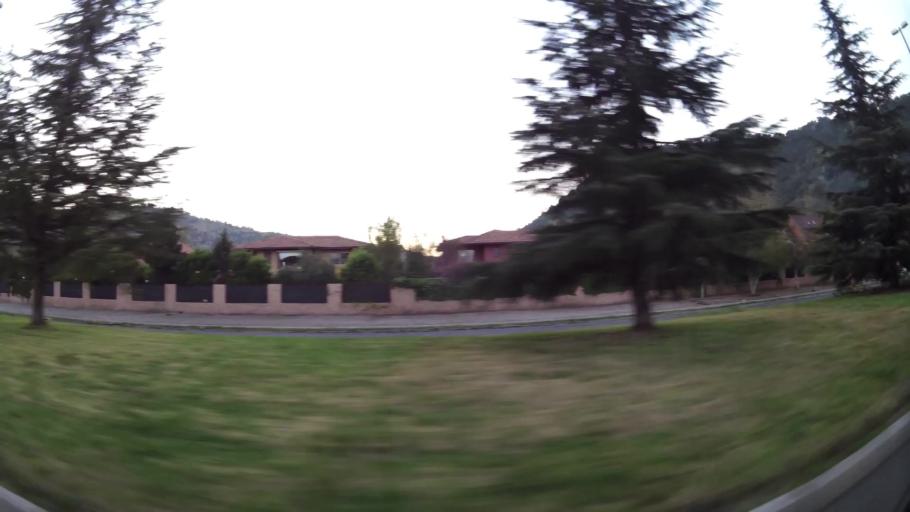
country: CL
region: Santiago Metropolitan
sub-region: Provincia de Chacabuco
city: Chicureo Abajo
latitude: -33.3214
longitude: -70.5539
